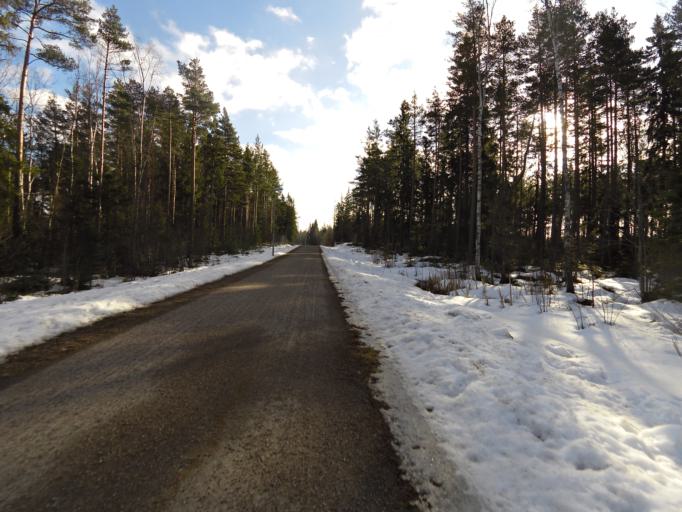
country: SE
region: Gaevleborg
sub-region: Gavle Kommun
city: Gavle
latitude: 60.6513
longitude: 17.2265
